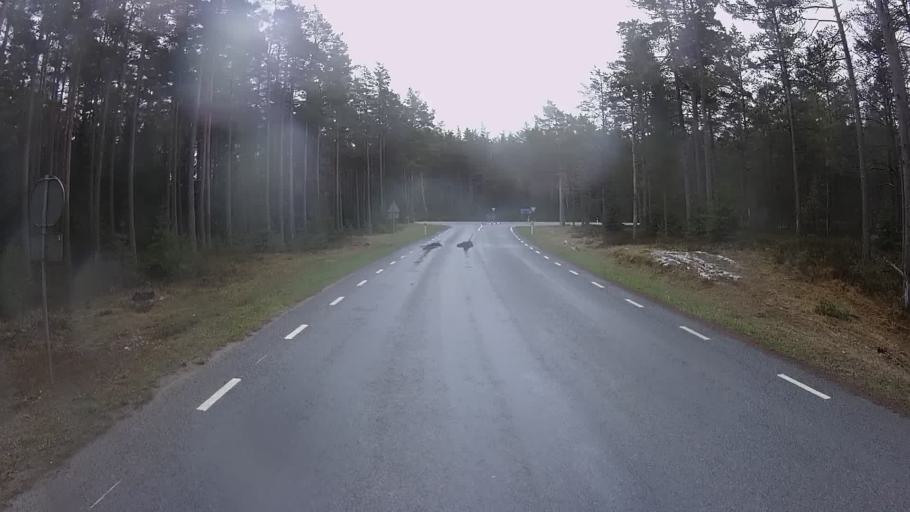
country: EE
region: Hiiumaa
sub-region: Kaerdla linn
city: Kardla
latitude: 58.9089
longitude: 22.3948
